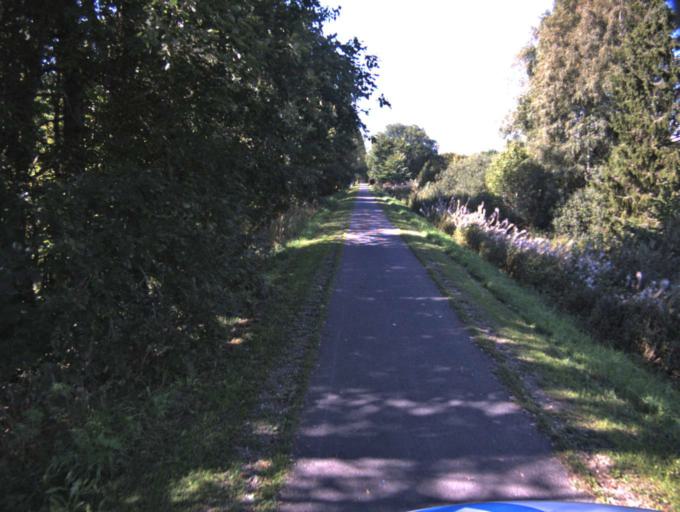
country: SE
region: Vaestra Goetaland
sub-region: Ulricehamns Kommun
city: Ulricehamn
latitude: 57.8010
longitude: 13.3743
